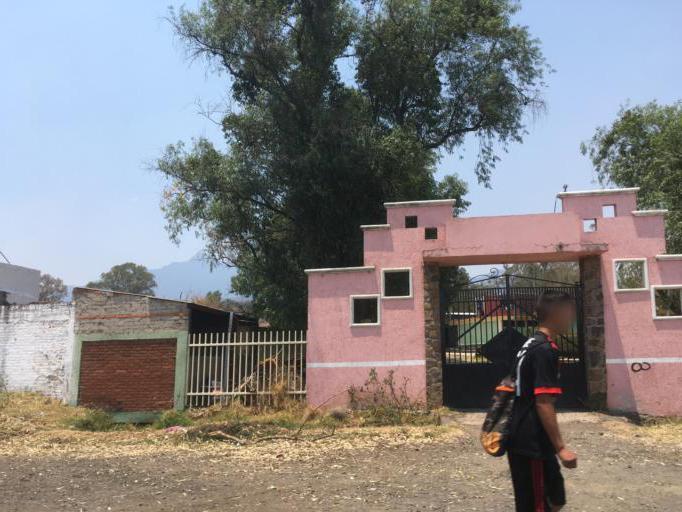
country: MX
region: Michoacan
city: Quiroga
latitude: 19.6669
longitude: -101.5319
